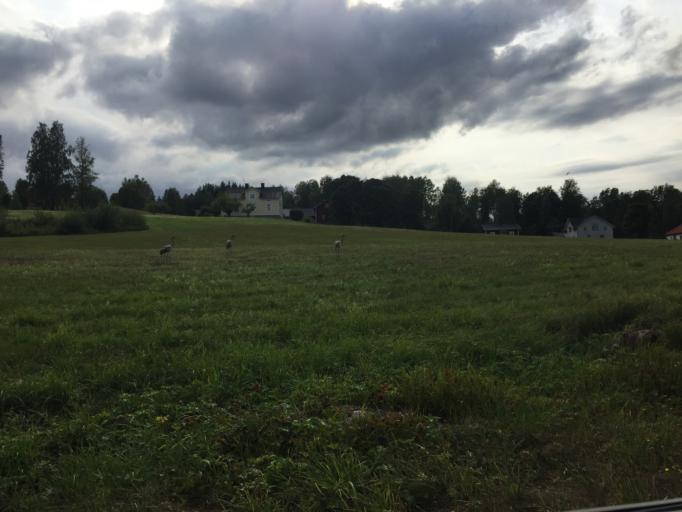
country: SE
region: Vaermland
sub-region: Filipstads Kommun
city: Lesjofors
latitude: 60.0249
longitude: 14.1127
